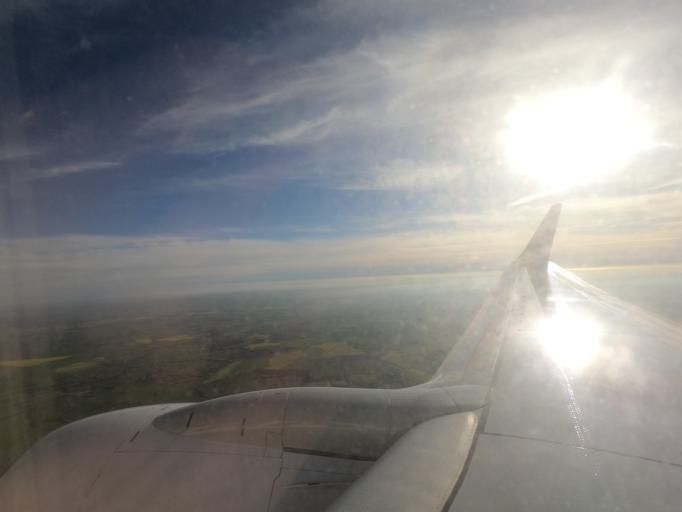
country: GB
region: England
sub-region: Essex
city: Great Yeldham
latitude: 52.0098
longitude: 0.5201
